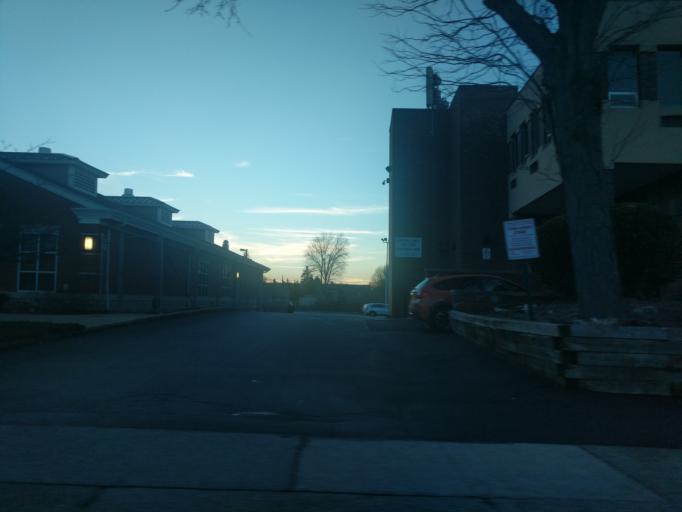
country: US
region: New York
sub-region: Nassau County
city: North Wantagh
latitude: 40.6924
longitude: -73.5080
